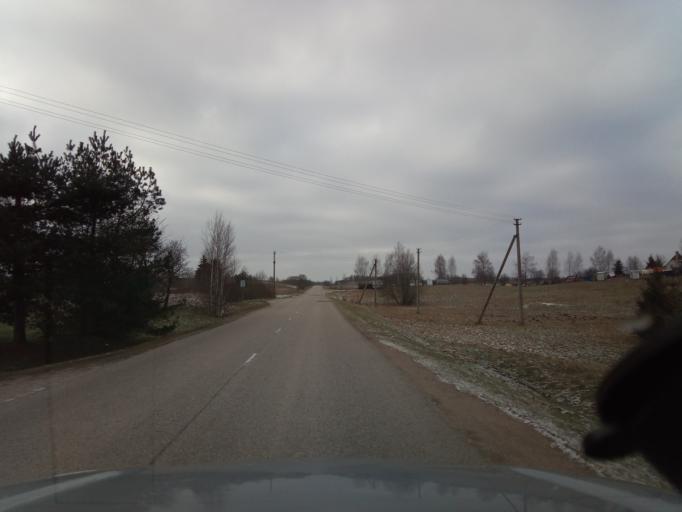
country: LT
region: Alytaus apskritis
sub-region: Alytaus rajonas
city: Daugai
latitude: 54.3514
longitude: 24.3248
